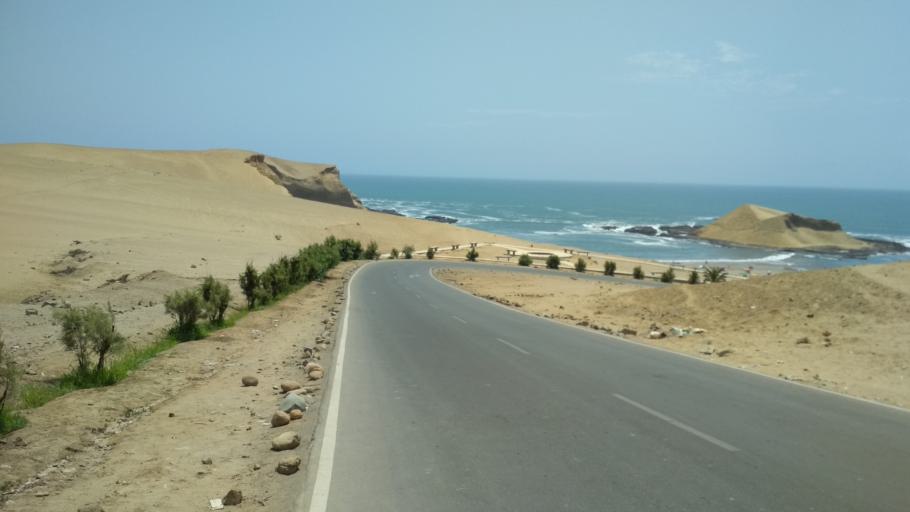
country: PE
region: Lima
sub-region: Barranca
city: Puerto Supe
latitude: -10.8085
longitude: -77.7475
